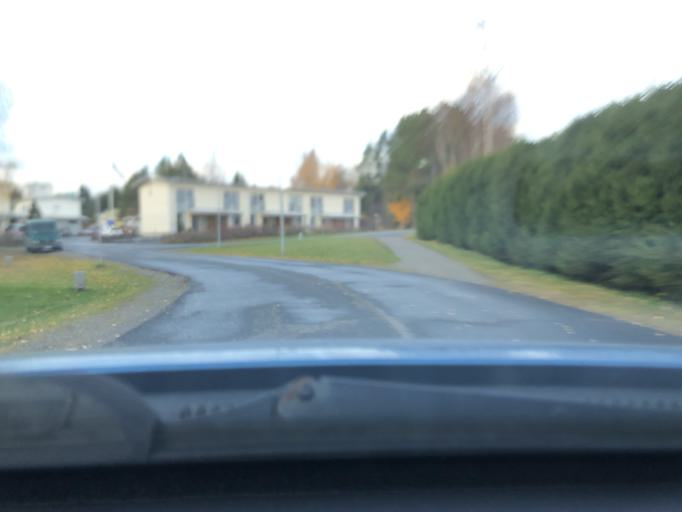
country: FI
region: Pirkanmaa
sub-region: Tampere
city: Kangasala
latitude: 61.4697
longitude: 24.0297
